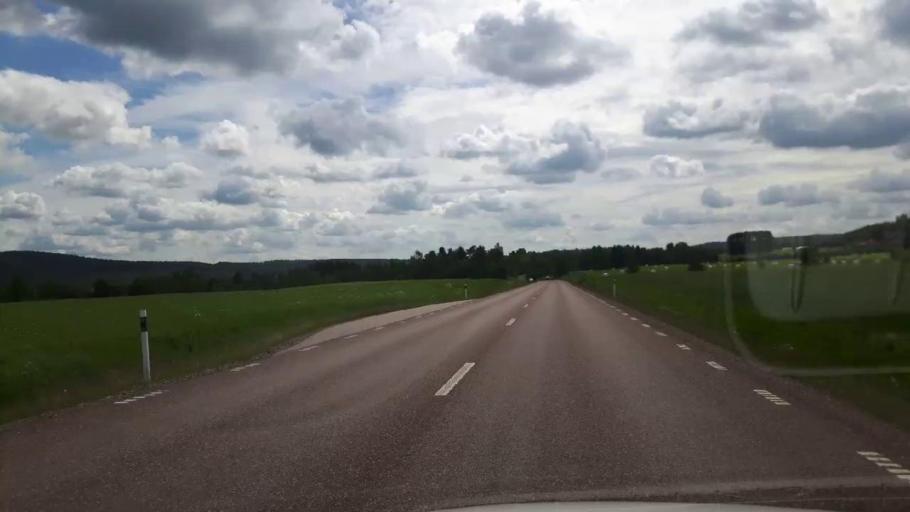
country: SE
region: Dalarna
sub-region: Hedemora Kommun
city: Langshyttan
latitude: 60.3870
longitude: 15.9042
